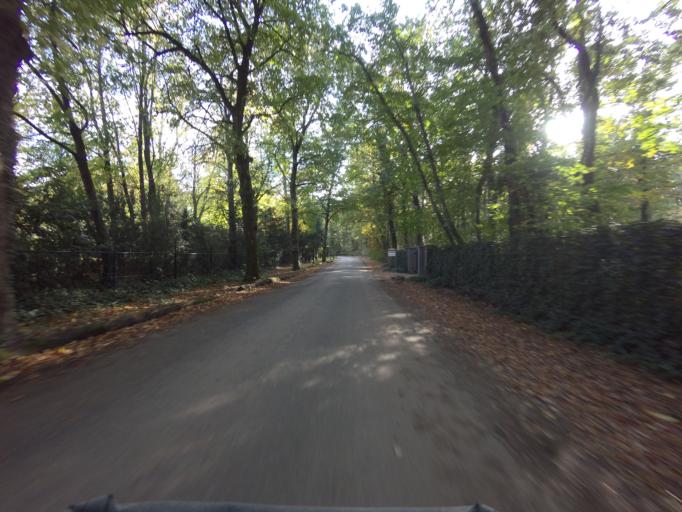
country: NL
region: North Holland
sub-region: Gemeente Naarden
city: Naarden
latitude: 52.3036
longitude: 5.1934
